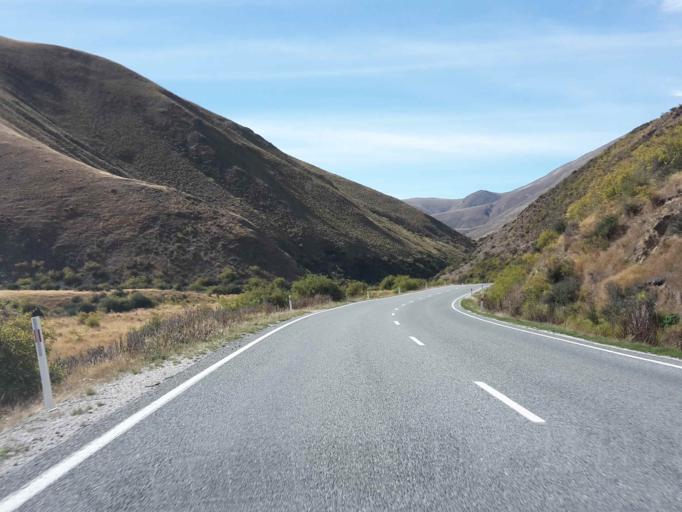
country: NZ
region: Otago
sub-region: Queenstown-Lakes District
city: Wanaka
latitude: -44.5621
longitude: 169.6684
